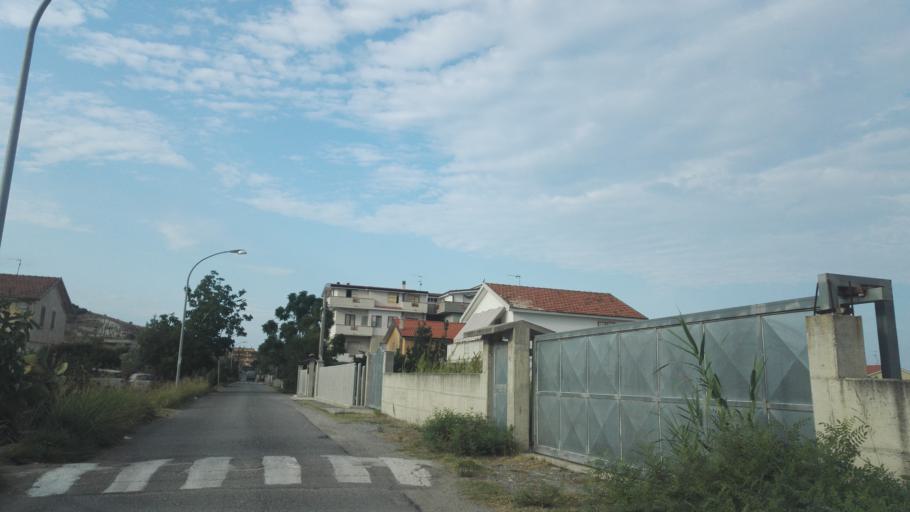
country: IT
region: Calabria
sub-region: Provincia di Reggio Calabria
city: Monasterace Marina
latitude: 38.4298
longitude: 16.5685
